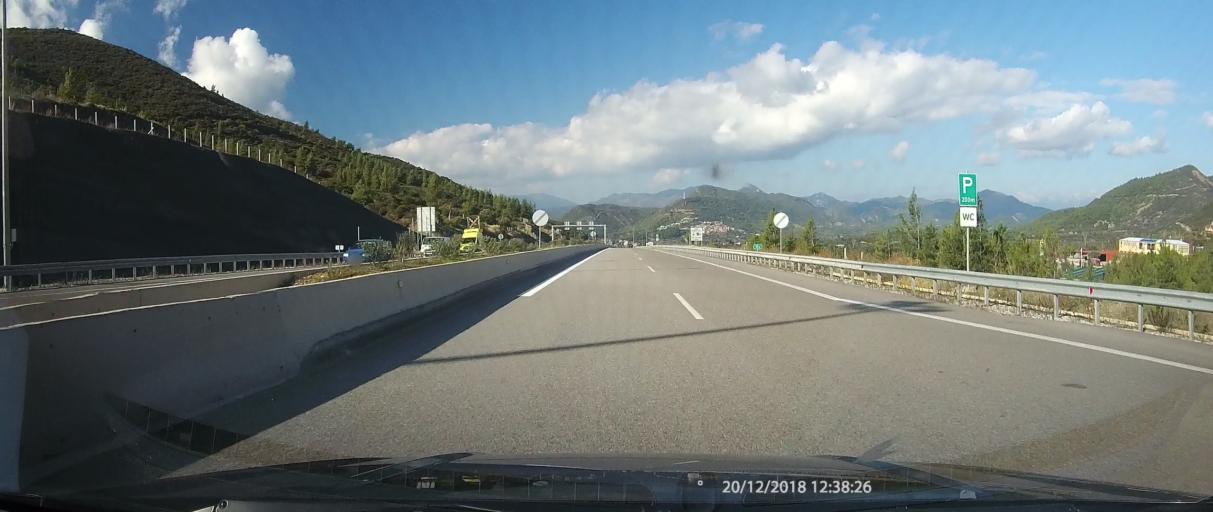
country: GR
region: West Greece
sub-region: Nomos Aitolias kai Akarnanias
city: Galatas
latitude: 38.3601
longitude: 21.6556
